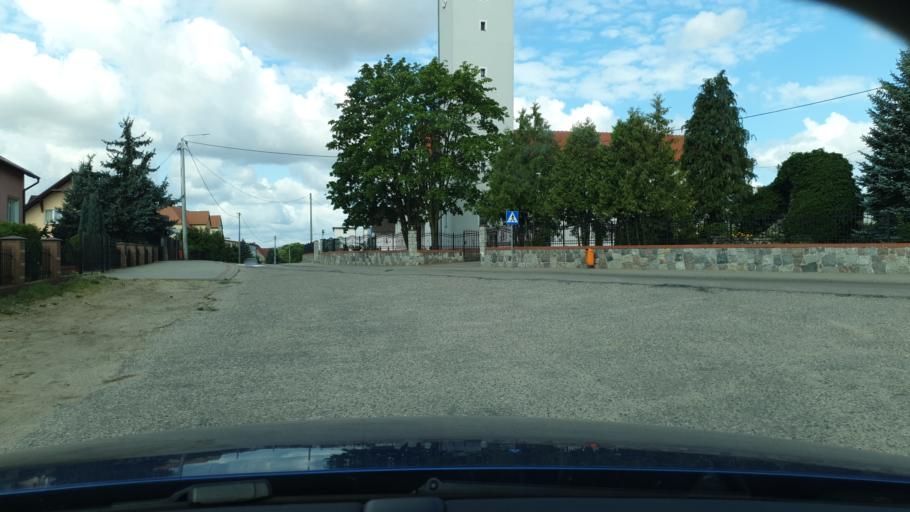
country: PL
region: Pomeranian Voivodeship
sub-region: Powiat czluchowski
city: Przechlewo
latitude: 53.8064
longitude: 17.3426
